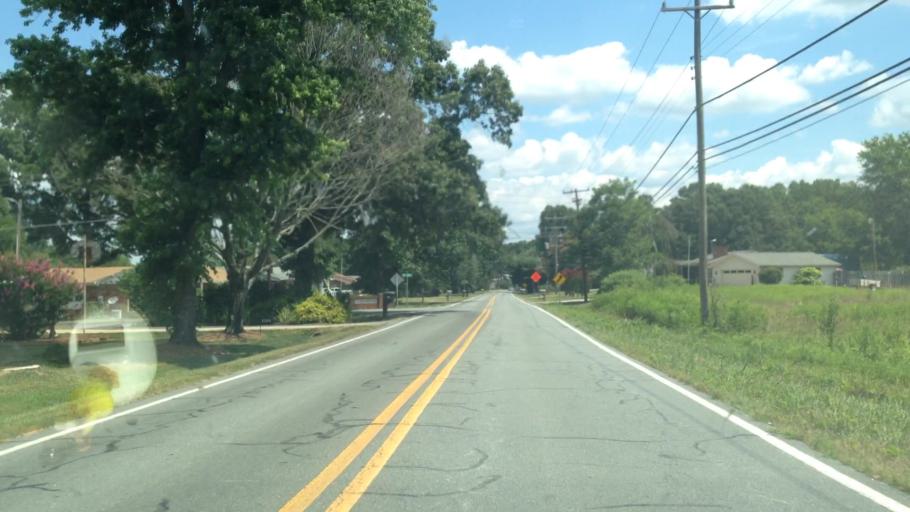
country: US
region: North Carolina
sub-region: Forsyth County
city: Kernersville
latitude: 36.1506
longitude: -80.0626
